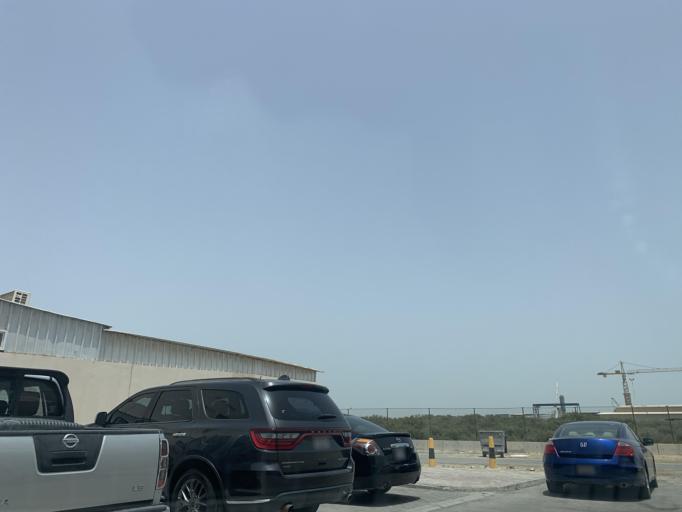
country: BH
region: Northern
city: Sitrah
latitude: 26.1470
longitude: 50.5915
